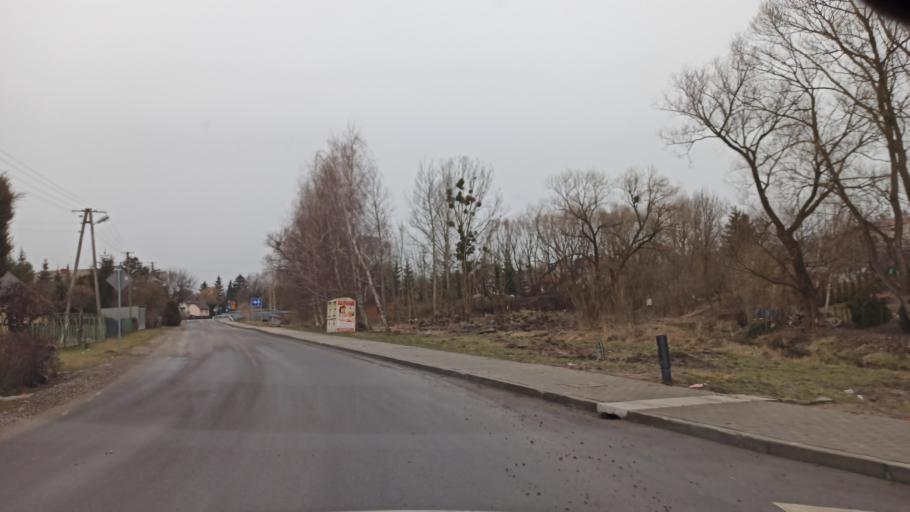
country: PL
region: Lublin Voivodeship
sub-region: Powiat lubelski
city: Wysokie
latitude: 50.9082
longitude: 22.6642
